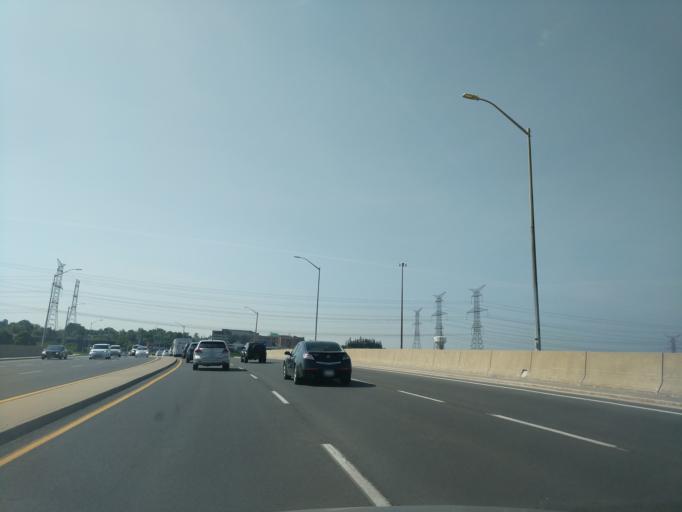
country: CA
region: Ontario
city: Markham
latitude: 43.8508
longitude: -79.3078
